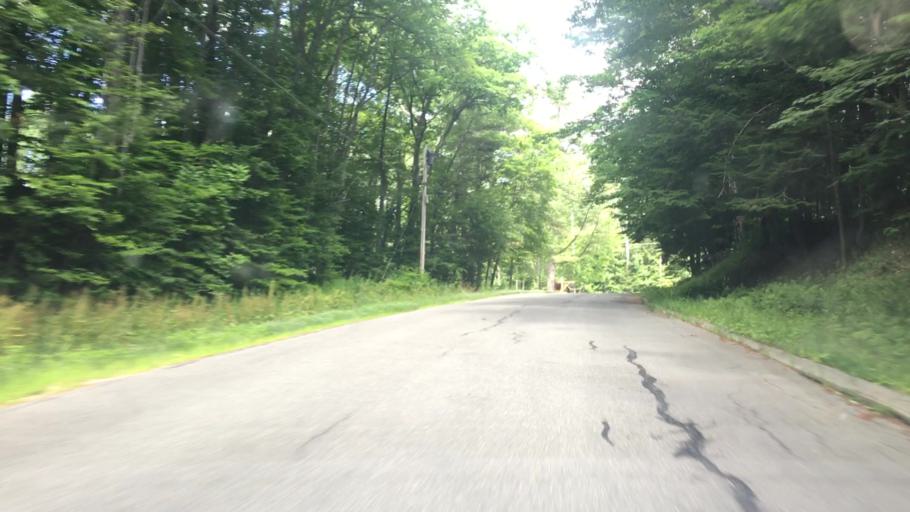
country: US
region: Maine
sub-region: Franklin County
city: Jay
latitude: 44.5380
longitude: -70.2205
